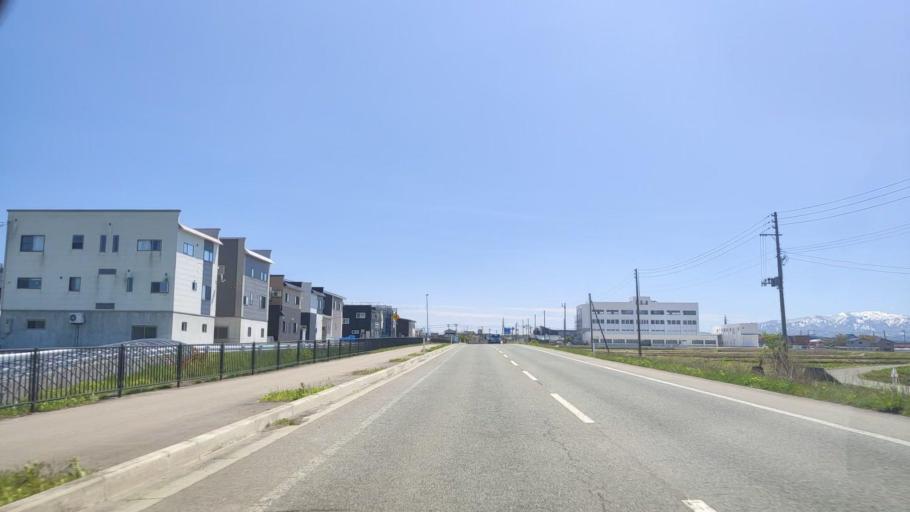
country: JP
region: Yamagata
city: Shinjo
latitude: 38.7541
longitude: 140.2944
